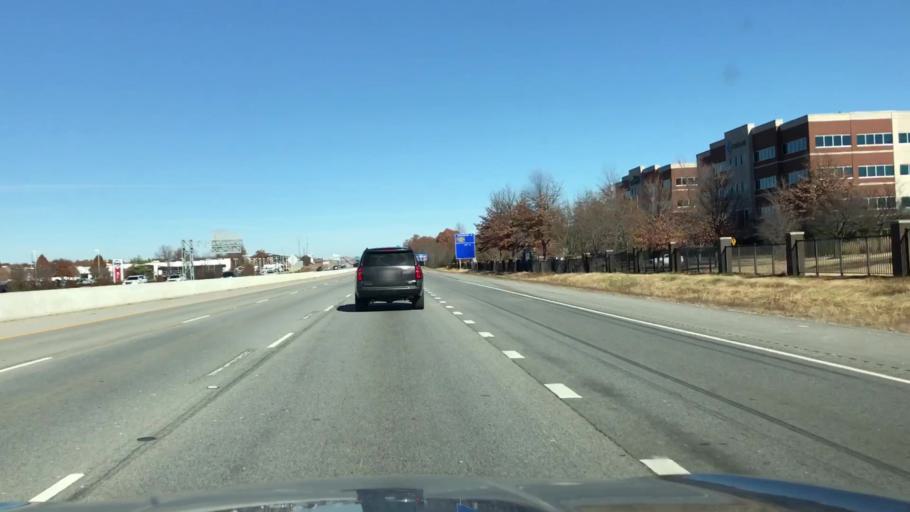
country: US
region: Arkansas
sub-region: Benton County
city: Bentonville
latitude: 36.3428
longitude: -94.1811
